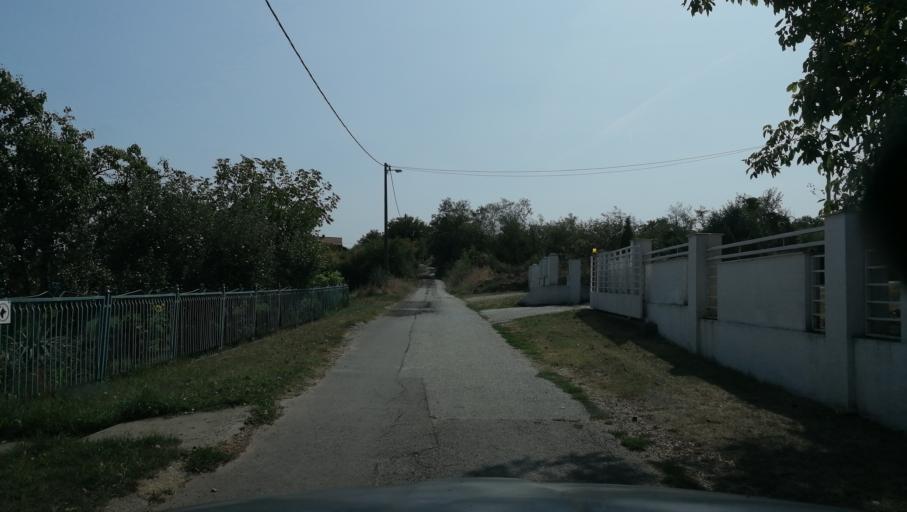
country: RS
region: Central Serbia
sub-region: Belgrade
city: Zvezdara
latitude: 44.6909
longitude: 20.5550
